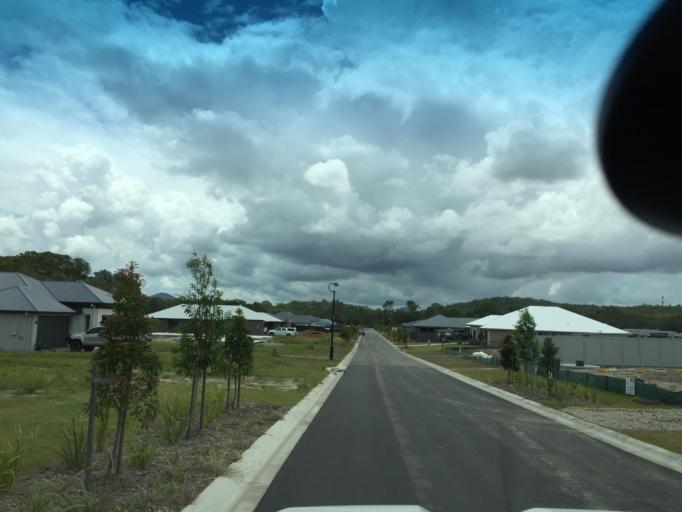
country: AU
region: Queensland
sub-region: Moreton Bay
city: Caboolture
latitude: -27.0438
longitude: 152.9258
